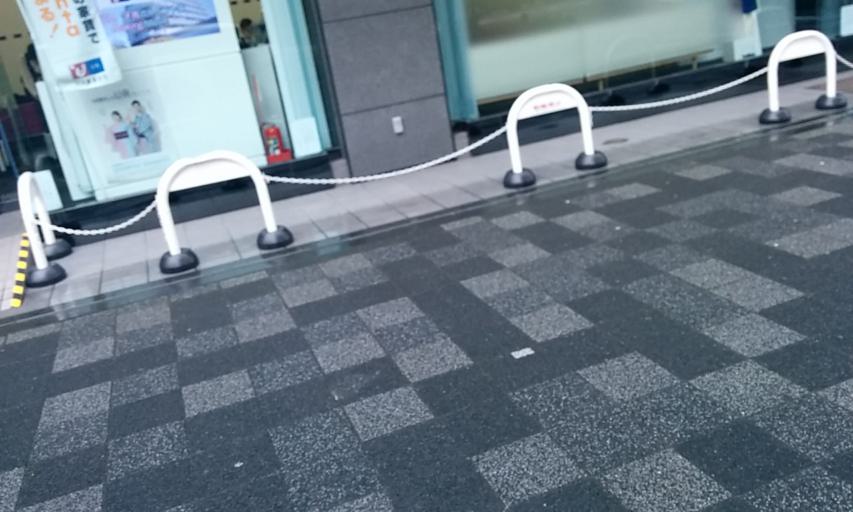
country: JP
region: Kyoto
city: Kyoto
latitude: 35.0116
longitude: 135.7577
